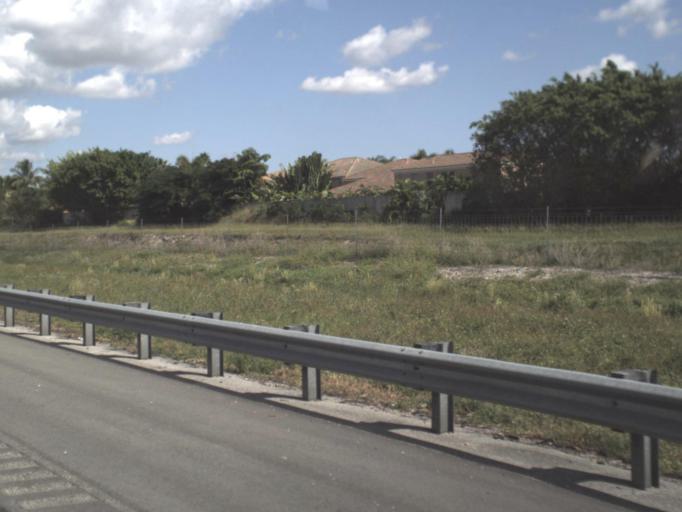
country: US
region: Florida
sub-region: Palm Beach County
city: Kings Point
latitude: 26.4015
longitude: -80.1712
